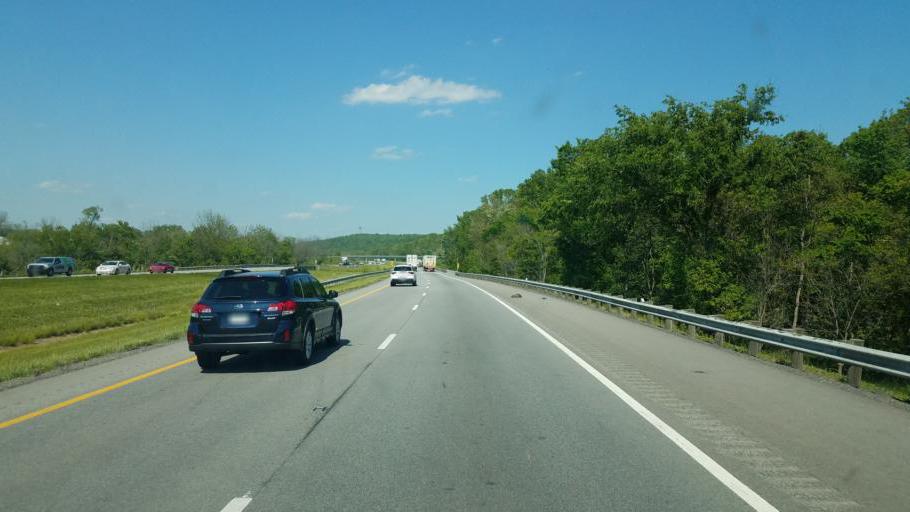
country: US
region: Ohio
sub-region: Muskingum County
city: New Concord
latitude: 39.9860
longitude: -81.6812
